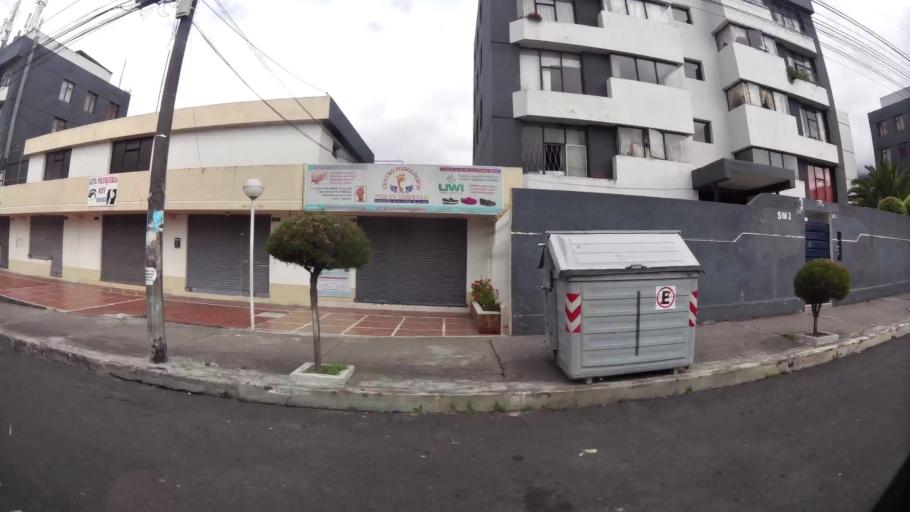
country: EC
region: Pichincha
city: Quito
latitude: -0.1294
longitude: -78.4962
